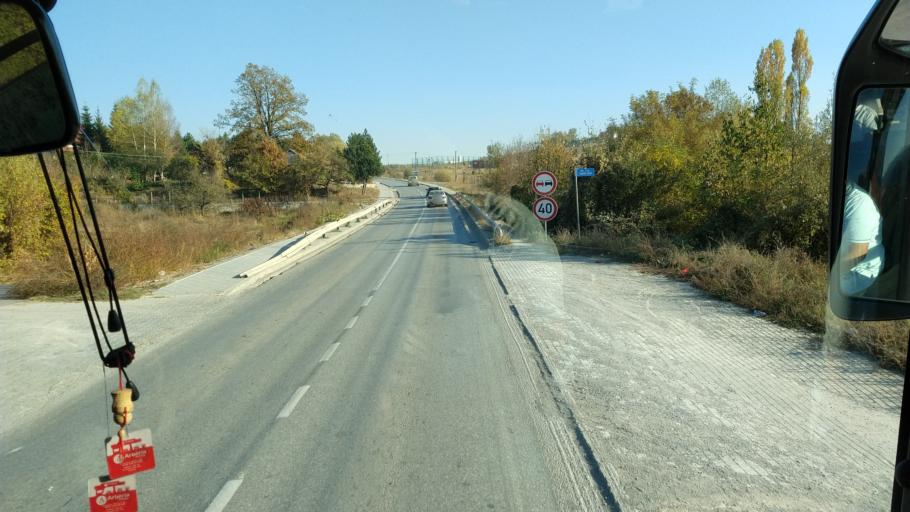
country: XK
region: Ferizaj
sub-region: Komuna e Shtimes
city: Shtime
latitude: 42.4391
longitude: 21.0184
